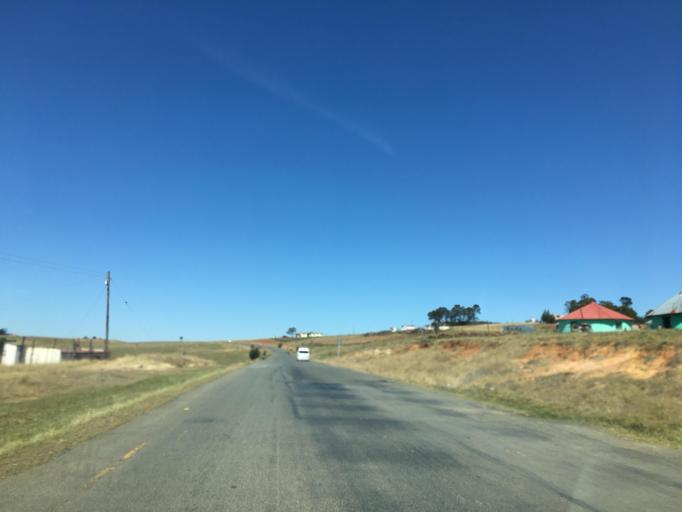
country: ZA
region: Eastern Cape
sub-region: Chris Hani District Municipality
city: Cala
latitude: -31.5584
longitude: 27.8972
